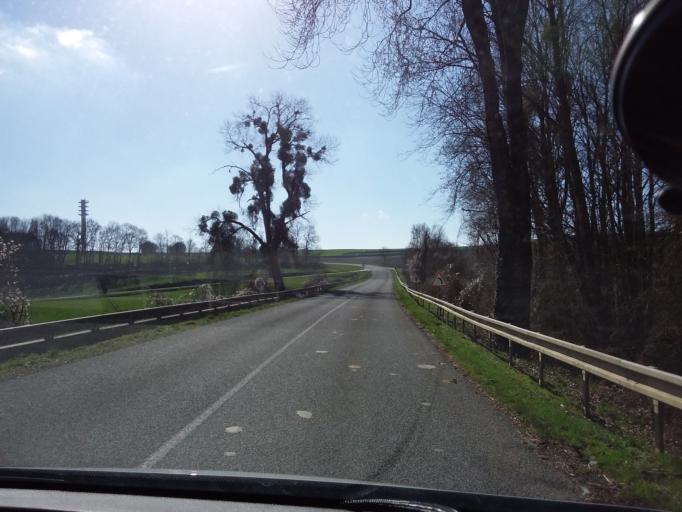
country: FR
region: Picardie
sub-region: Departement de l'Aisne
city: Montcornet
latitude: 49.7212
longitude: 4.0149
